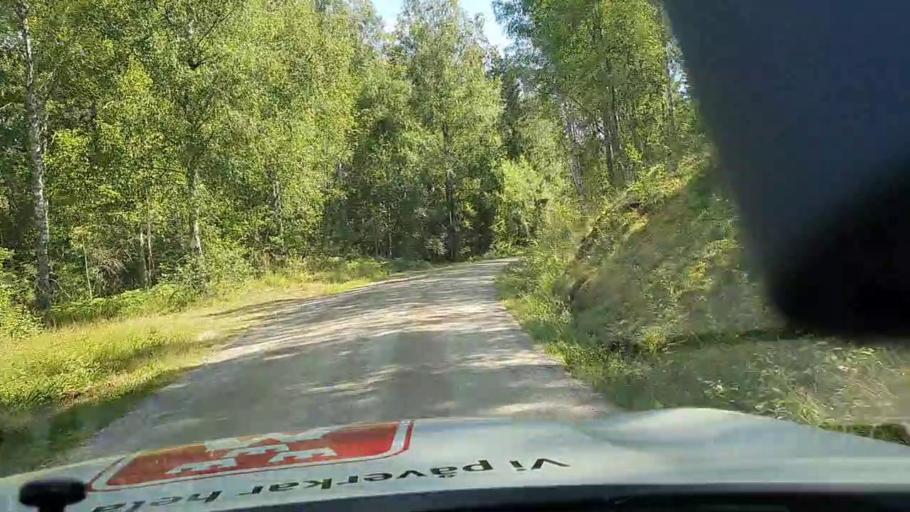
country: SE
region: Soedermanland
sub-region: Strangnas Kommun
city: Akers Styckebruk
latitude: 59.2090
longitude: 16.9156
